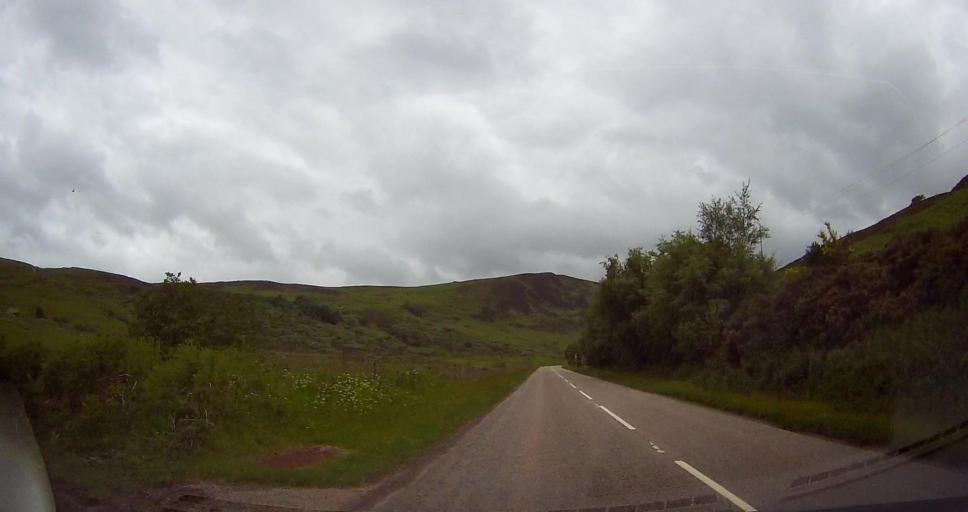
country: GB
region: Scotland
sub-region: Highland
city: Dornoch
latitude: 58.0064
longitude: -4.2609
